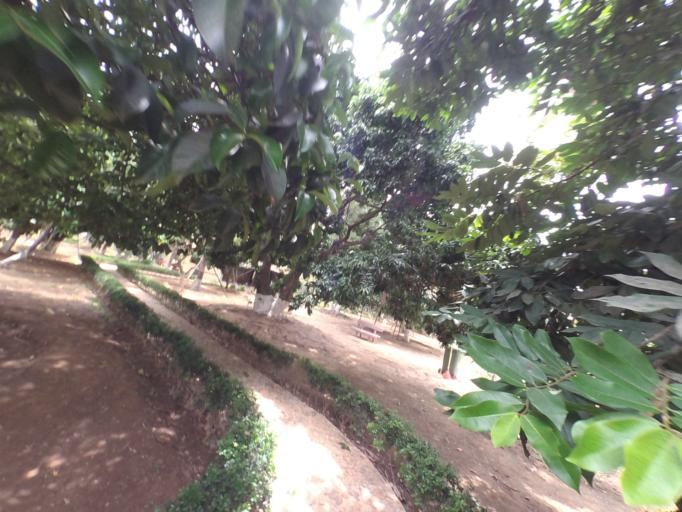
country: VN
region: Thua Thien-Hue
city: Hue
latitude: 16.4555
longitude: 107.5534
